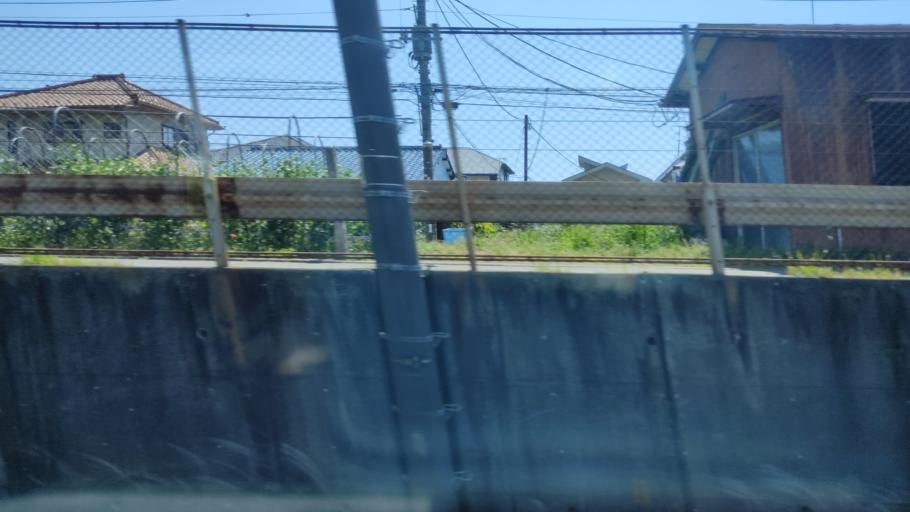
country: JP
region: Kanagawa
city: Ninomiya
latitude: 35.3017
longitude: 139.2649
